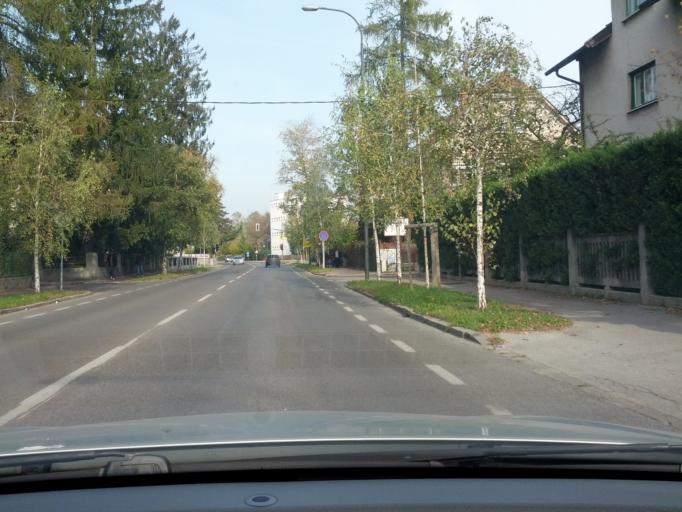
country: SI
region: Ljubljana
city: Ljubljana
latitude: 46.0697
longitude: 14.5179
